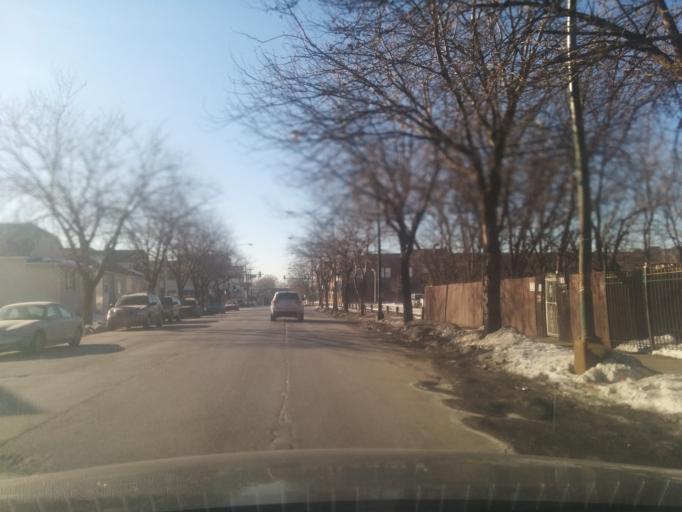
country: US
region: Illinois
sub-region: Cook County
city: Elmwood Park
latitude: 41.9189
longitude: -87.7755
